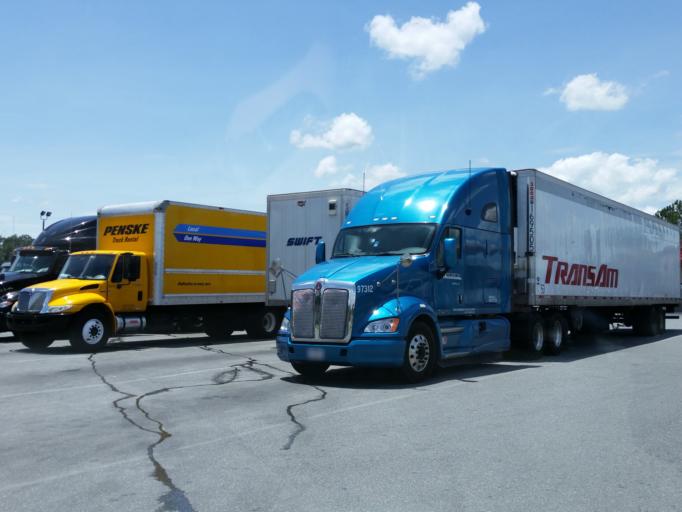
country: US
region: Florida
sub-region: Alachua County
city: High Springs
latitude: 29.9952
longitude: -82.5979
